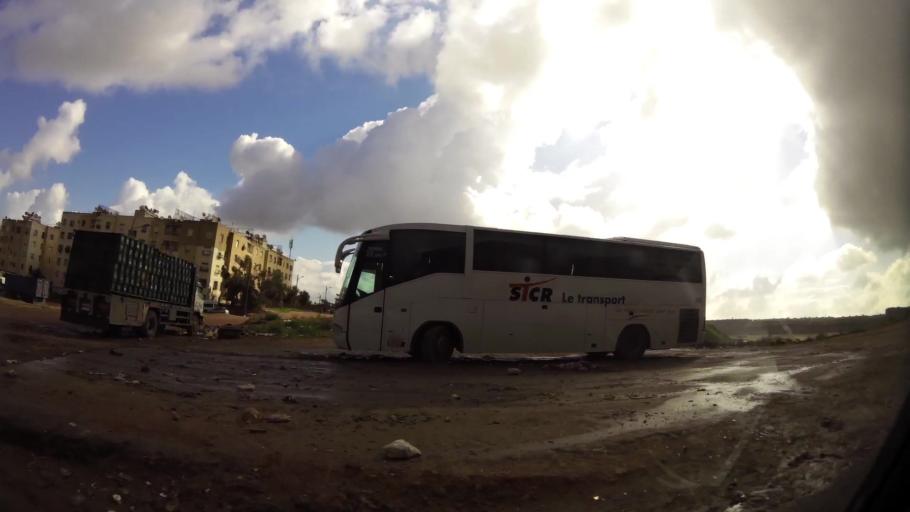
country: MA
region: Grand Casablanca
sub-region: Mediouna
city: Tit Mellil
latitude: 33.5837
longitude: -7.5210
